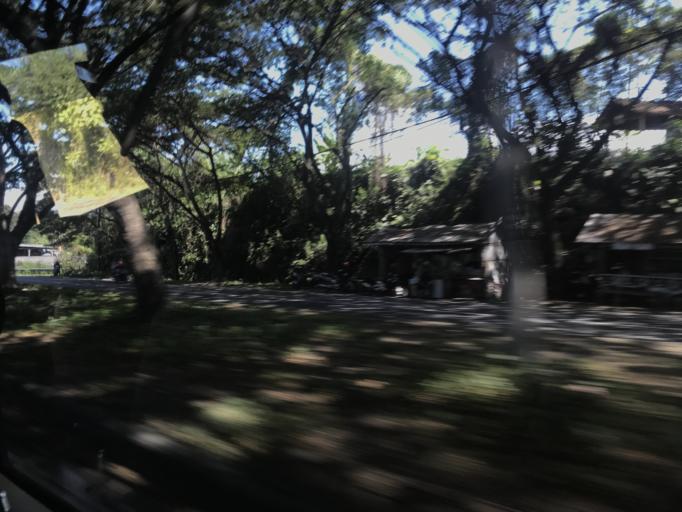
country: ID
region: Bali
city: Dawan
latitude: -8.5573
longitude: 115.4300
